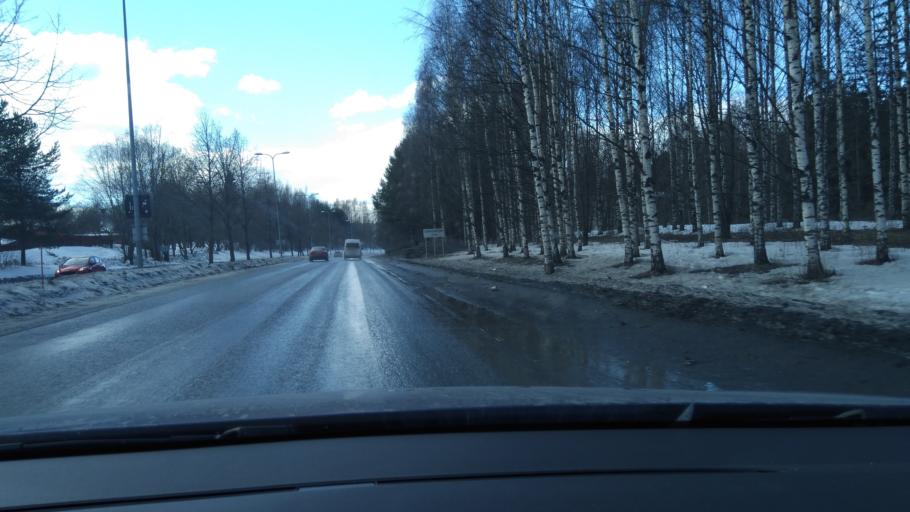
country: FI
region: Pirkanmaa
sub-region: Tampere
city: Tampere
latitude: 61.4982
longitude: 23.8147
